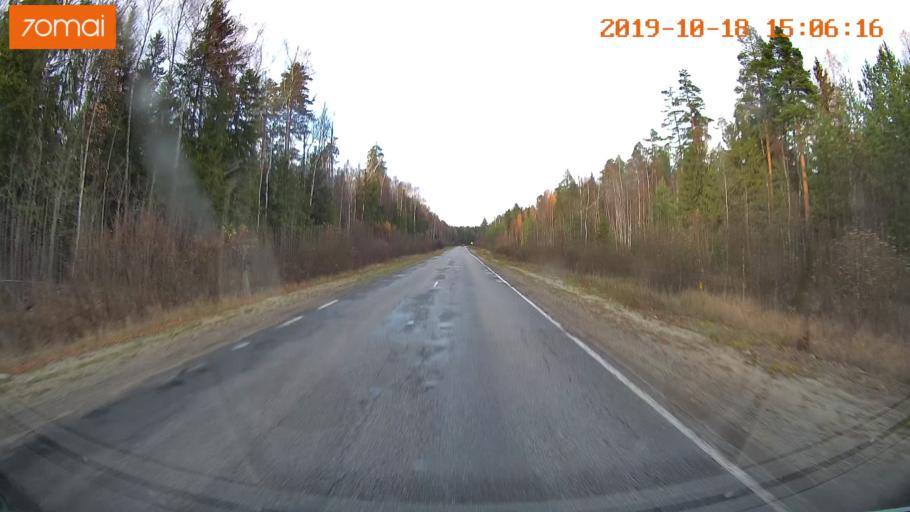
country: RU
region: Vladimir
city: Gus'-Khrustal'nyy
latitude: 55.5276
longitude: 40.5774
